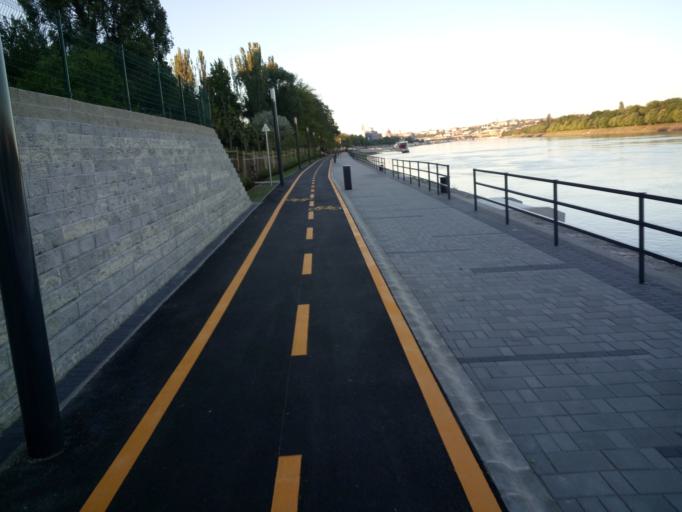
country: HU
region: Budapest
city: Budapest III. keruelet
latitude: 47.5320
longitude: 19.0568
